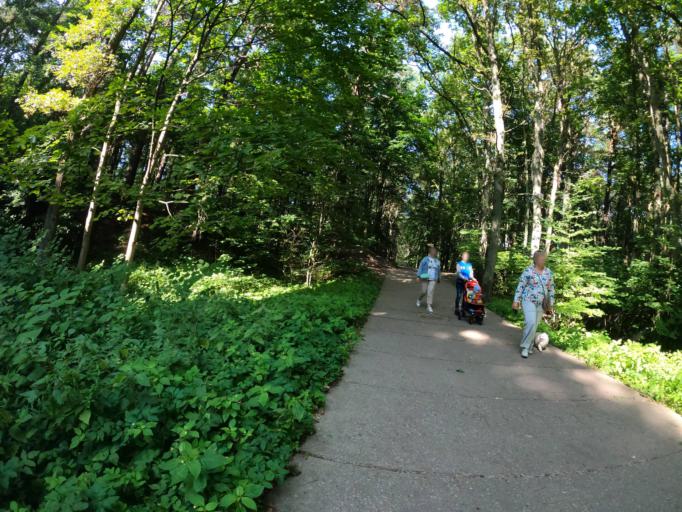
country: RU
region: Kaliningrad
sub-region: Gorod Svetlogorsk
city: Svetlogorsk
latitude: 54.9341
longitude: 20.1594
